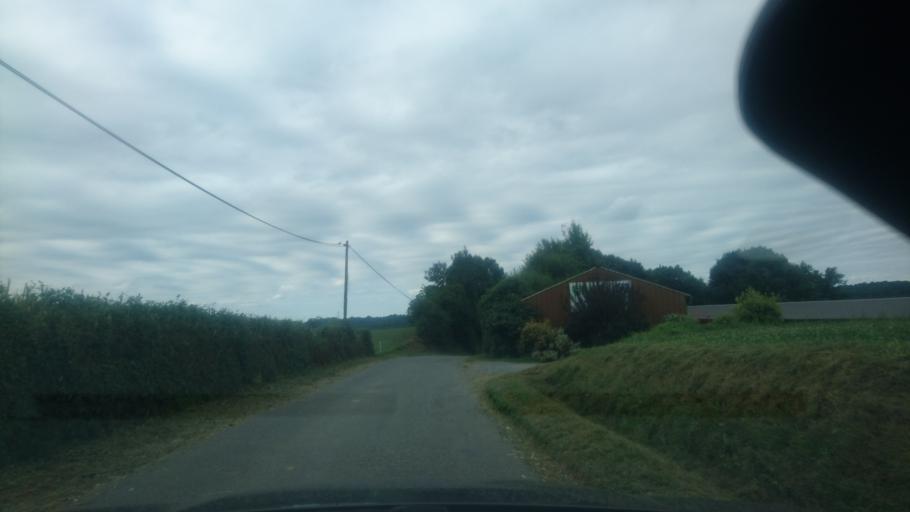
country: FR
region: Midi-Pyrenees
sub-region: Departement des Hautes-Pyrenees
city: Odos
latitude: 43.1413
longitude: 0.0414
